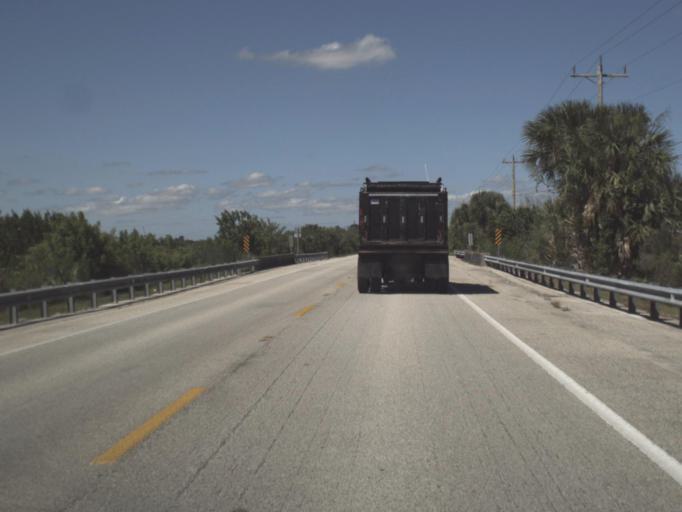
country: US
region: Florida
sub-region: Collier County
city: Marco
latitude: 25.9379
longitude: -81.4607
